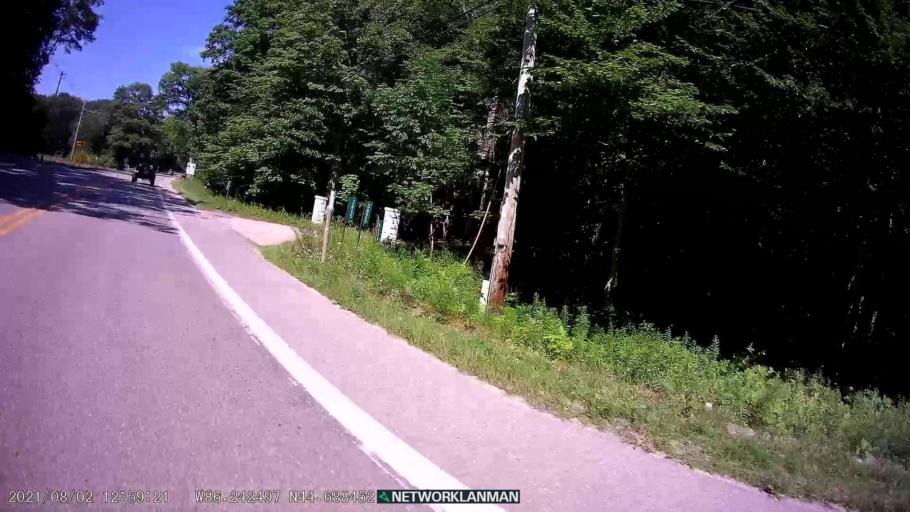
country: US
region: Michigan
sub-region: Benzie County
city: Frankfort
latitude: 44.6886
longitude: -86.2425
